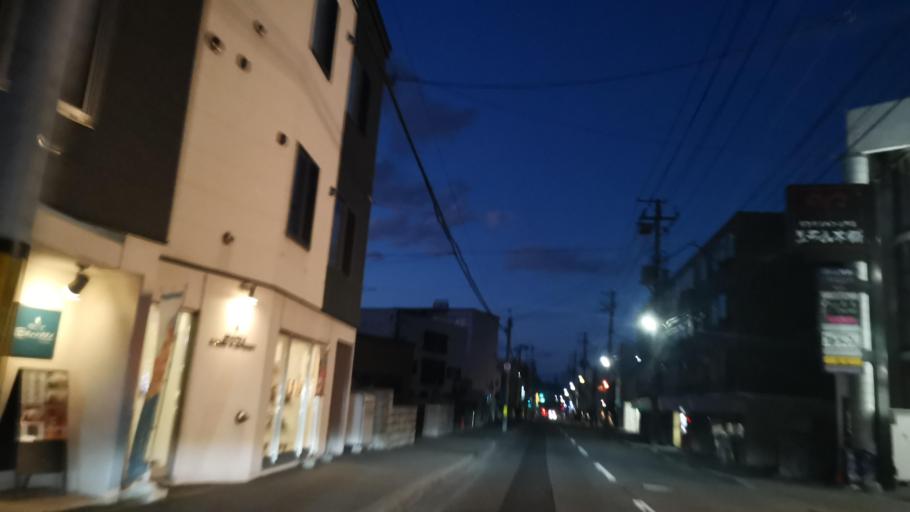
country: JP
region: Hokkaido
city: Sapporo
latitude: 43.0156
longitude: 141.3684
